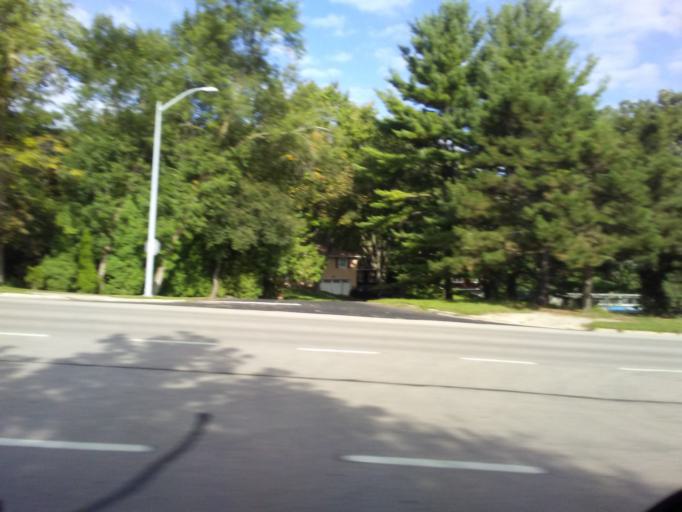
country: US
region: Wisconsin
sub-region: Dane County
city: Shorewood Hills
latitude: 43.0723
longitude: -89.4681
